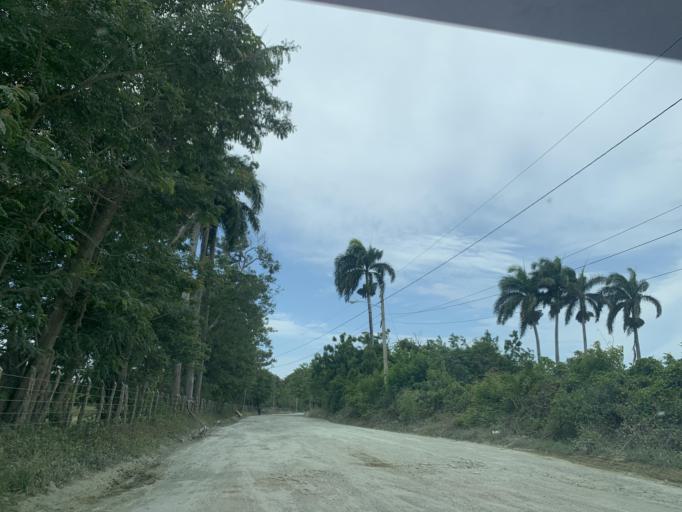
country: DO
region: Puerto Plata
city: Imbert
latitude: 19.8210
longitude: -70.7822
